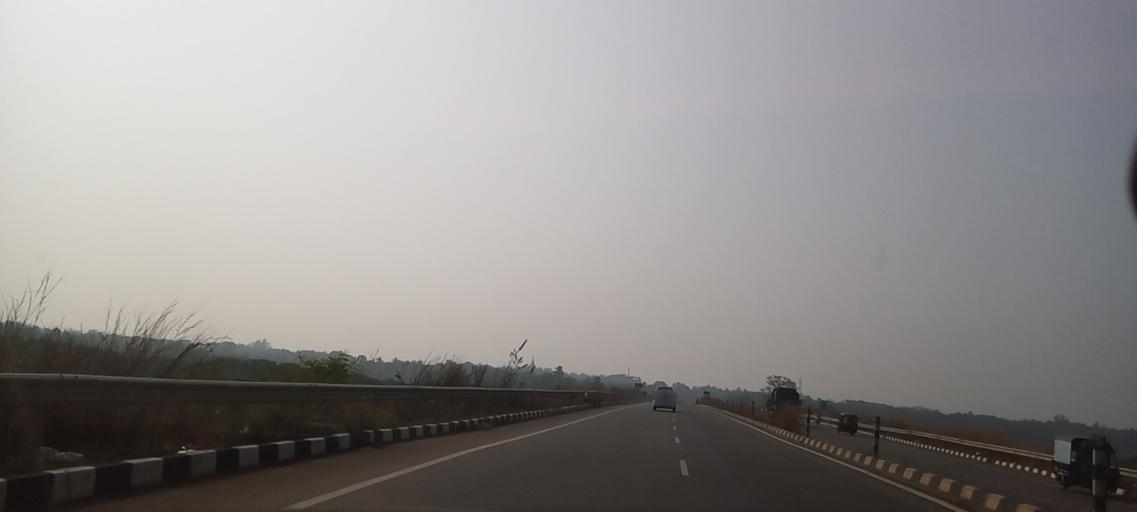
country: IN
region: Karnataka
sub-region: Udupi
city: Coondapoor
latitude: 13.6632
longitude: 74.7059
